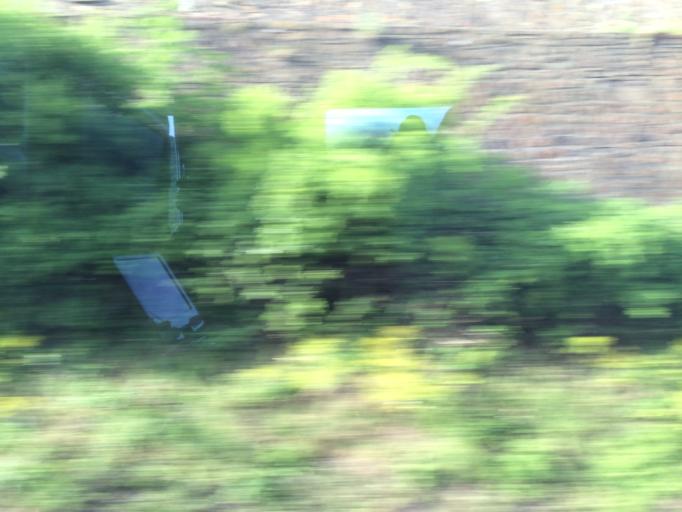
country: DE
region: Rheinland-Pfalz
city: Bingen am Rhein
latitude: 49.9746
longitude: 7.8818
